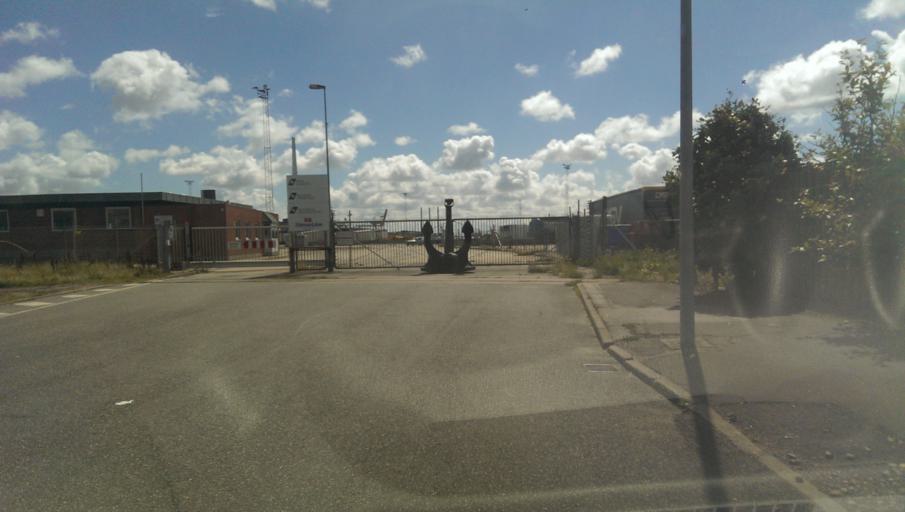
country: DK
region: South Denmark
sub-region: Esbjerg Kommune
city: Esbjerg
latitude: 55.4641
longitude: 8.4354
